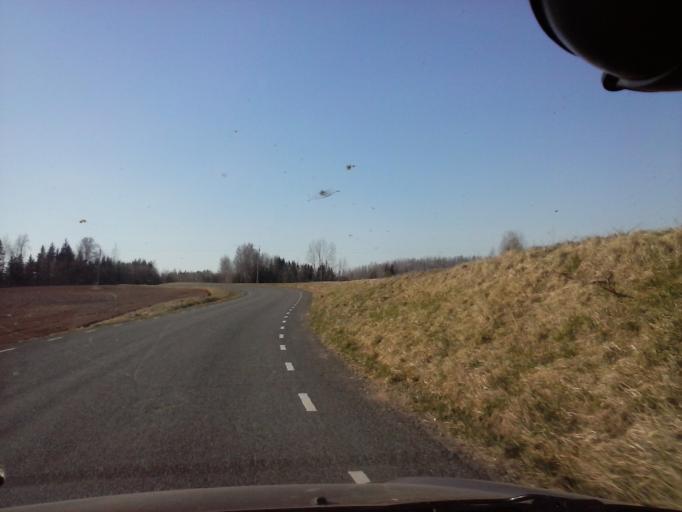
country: EE
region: Tartu
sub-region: UElenurme vald
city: Ulenurme
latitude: 58.1591
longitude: 26.8517
